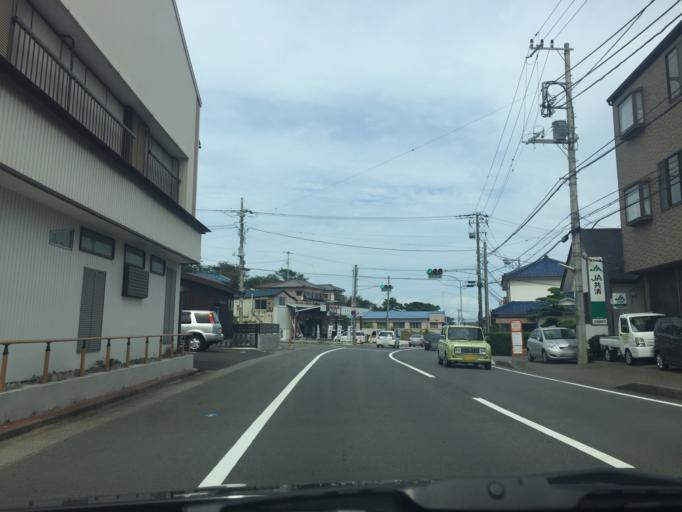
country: JP
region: Shizuoka
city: Shimoda
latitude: 34.7685
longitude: 139.0338
